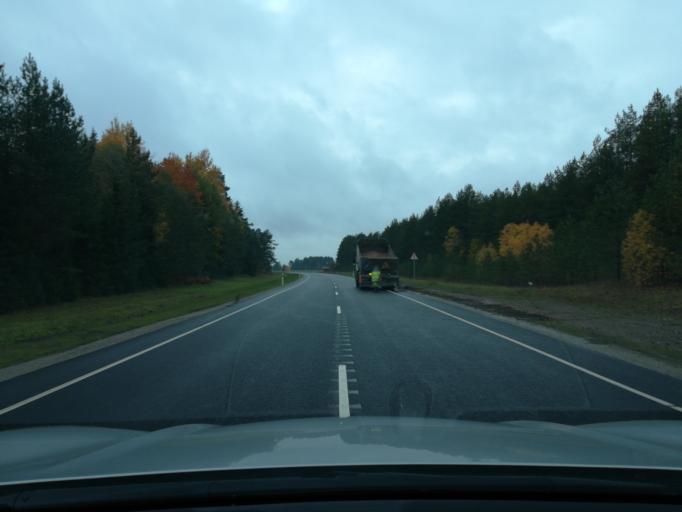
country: EE
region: Ida-Virumaa
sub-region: Johvi vald
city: Johvi
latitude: 59.1336
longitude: 27.3369
